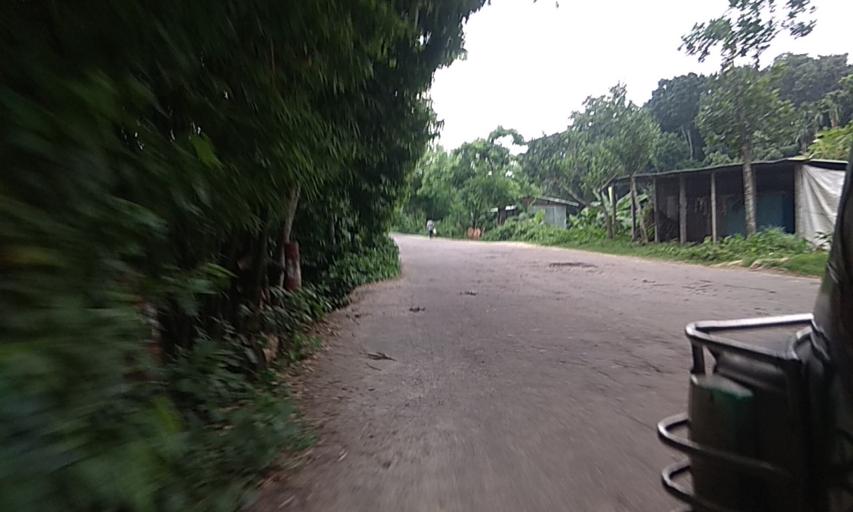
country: BD
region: Dhaka
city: Dohar
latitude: 23.4553
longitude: 90.0059
